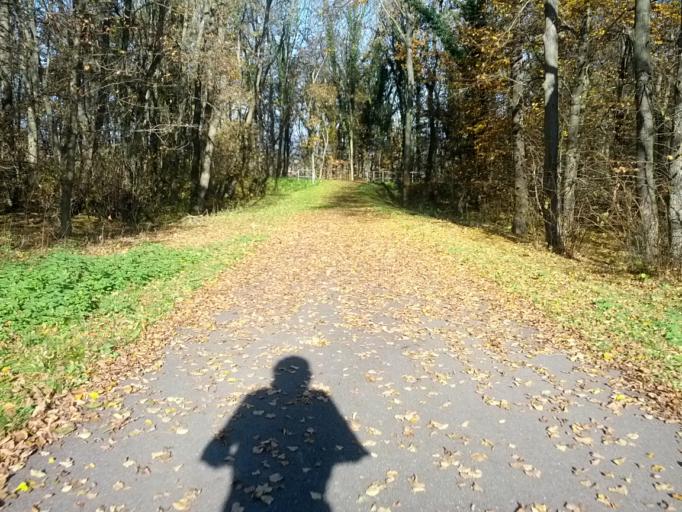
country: DE
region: Thuringia
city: Haina
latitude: 50.9933
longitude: 10.4932
